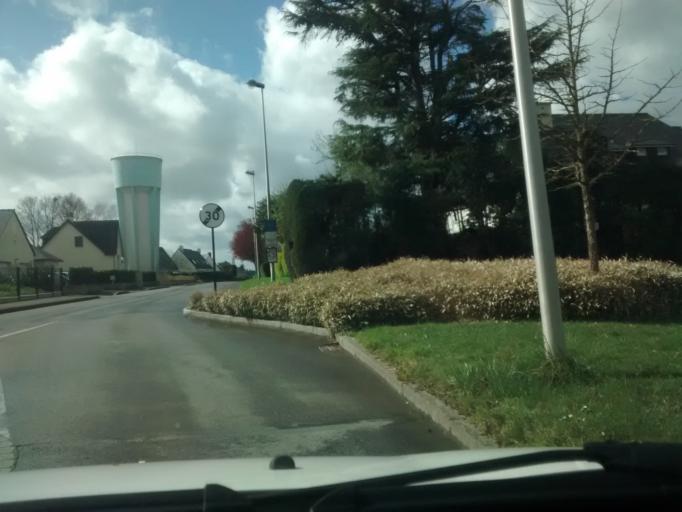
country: FR
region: Brittany
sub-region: Departement d'Ille-et-Vilaine
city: Acigne
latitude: 48.1394
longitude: -1.5323
